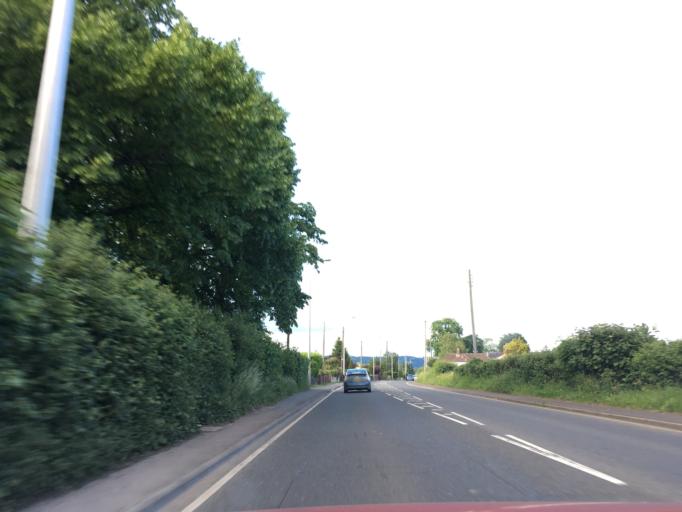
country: GB
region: England
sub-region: North Somerset
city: Churchill
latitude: 51.3356
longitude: -2.7924
